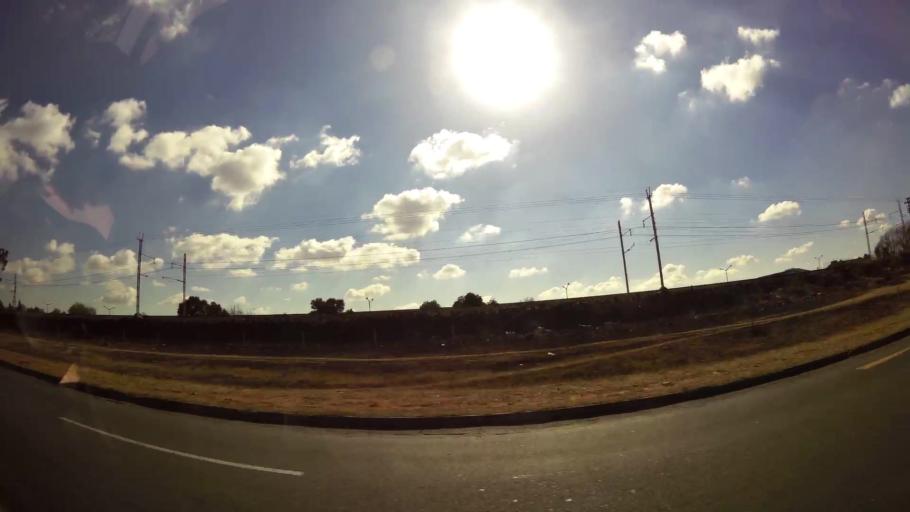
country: ZA
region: Gauteng
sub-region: City of Johannesburg Metropolitan Municipality
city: Roodepoort
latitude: -26.1269
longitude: 27.8286
